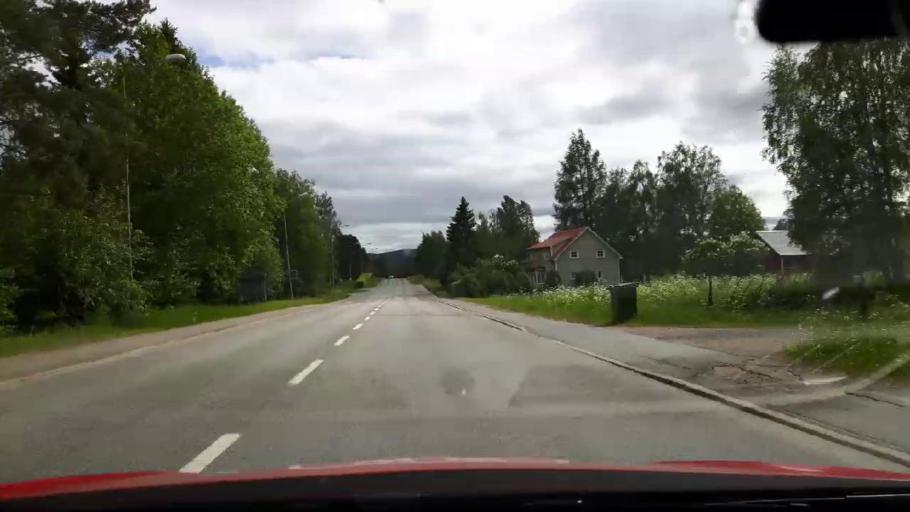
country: SE
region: Jaemtland
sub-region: Ragunda Kommun
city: Hammarstrand
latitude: 63.1011
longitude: 16.3577
